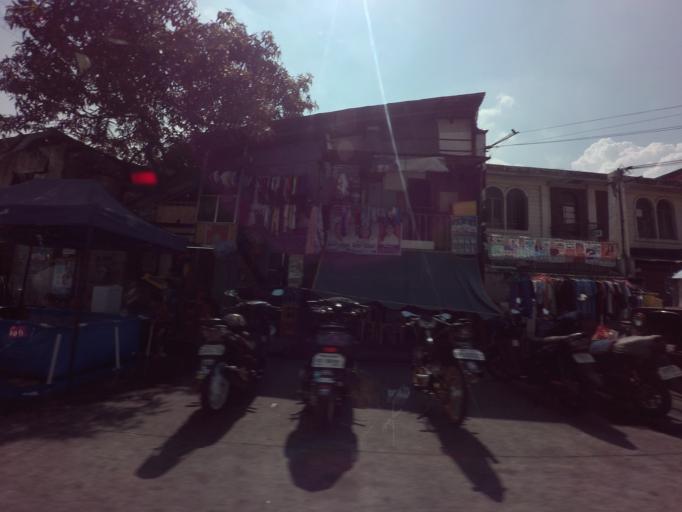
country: PH
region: Metro Manila
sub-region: Makati City
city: Makati City
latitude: 14.5684
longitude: 121.0126
